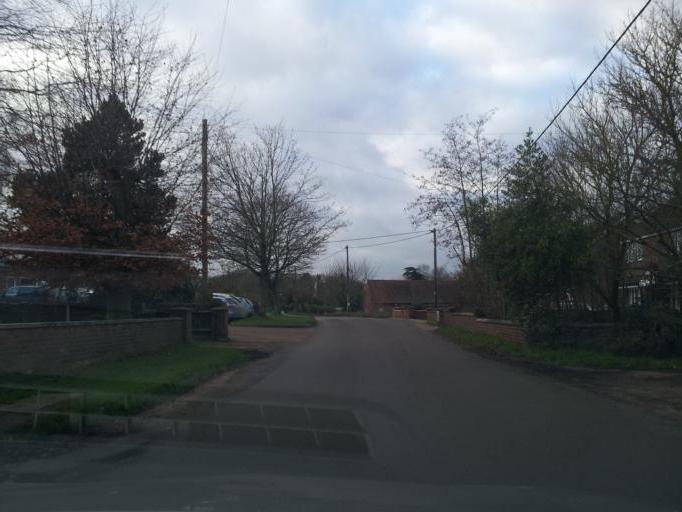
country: GB
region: England
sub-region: Norfolk
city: Lingwood
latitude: 52.6186
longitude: 1.4768
